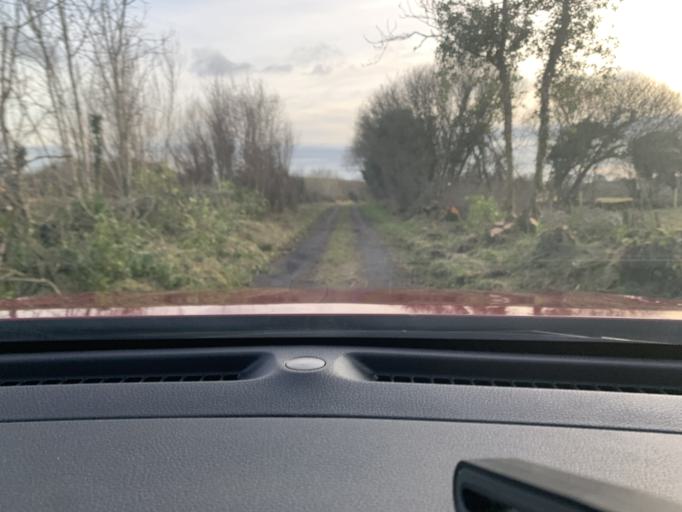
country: IE
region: Connaught
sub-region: Sligo
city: Strandhill
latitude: 54.1709
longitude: -8.6475
